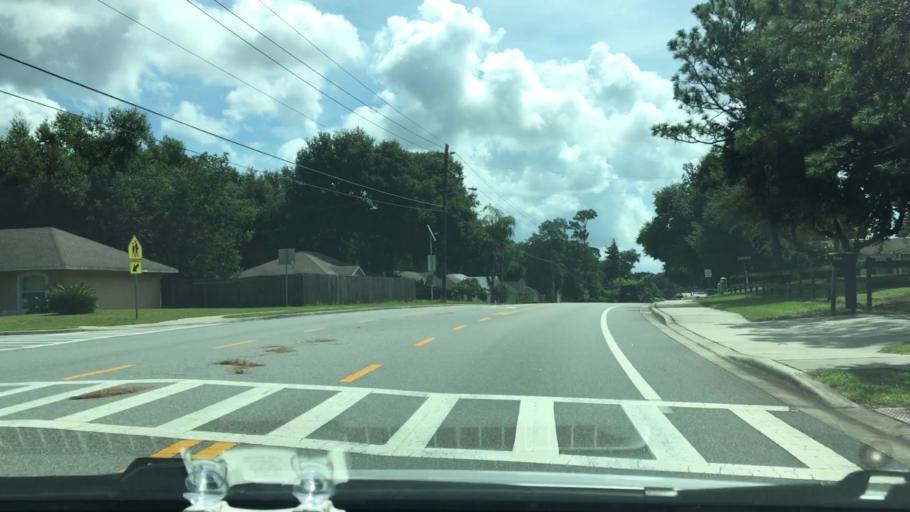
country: US
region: Florida
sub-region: Volusia County
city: Deltona
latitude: 28.8797
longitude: -81.1739
